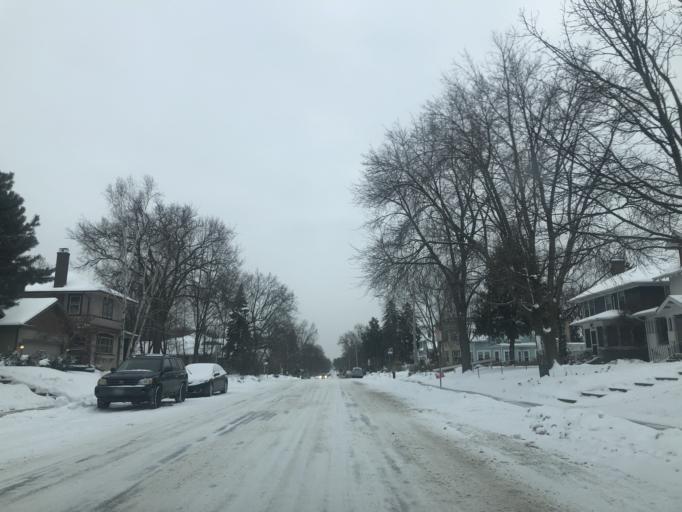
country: US
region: Minnesota
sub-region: Hennepin County
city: Richfield
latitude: 44.9292
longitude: -93.2909
